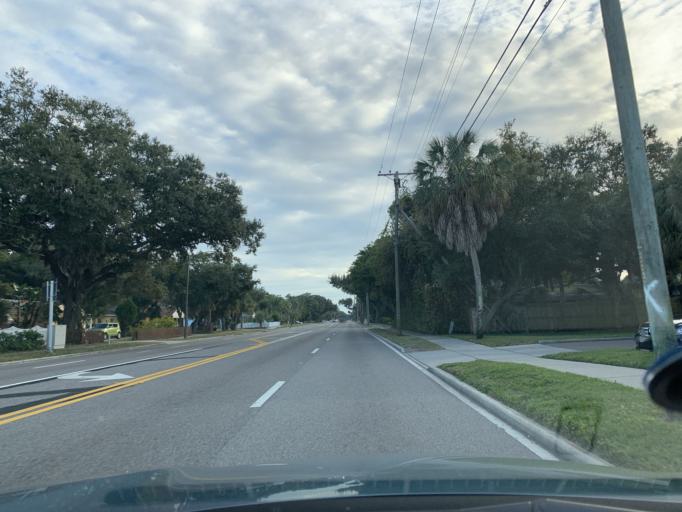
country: US
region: Florida
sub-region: Pinellas County
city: Bay Pines
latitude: 27.8063
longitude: -82.7539
